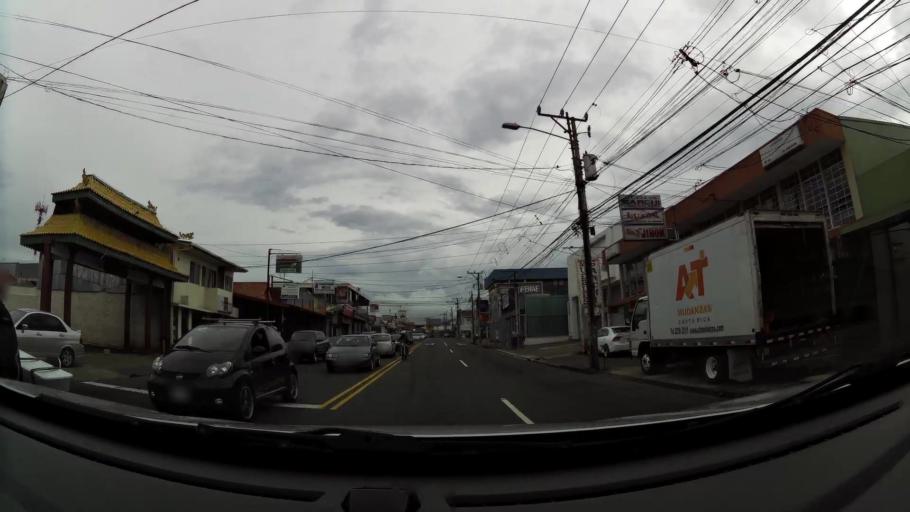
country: CR
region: San Jose
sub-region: Canton de Goicoechea
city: Guadalupe
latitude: 9.9485
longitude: -84.0502
